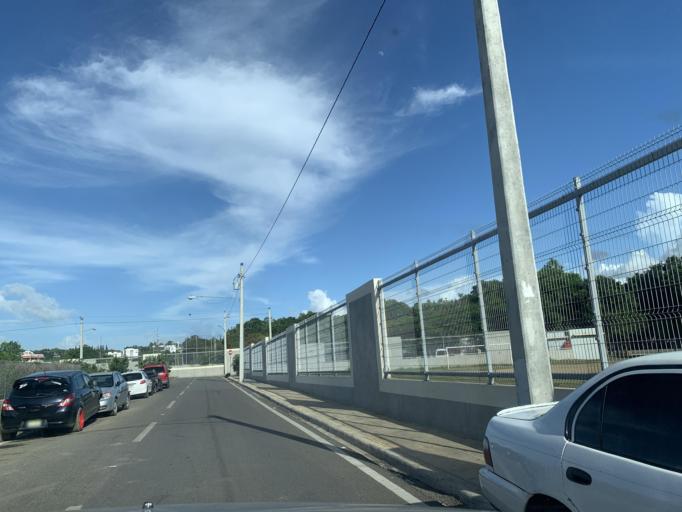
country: DO
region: Santiago
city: Santiago de los Caballeros
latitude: 19.4690
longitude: -70.6965
